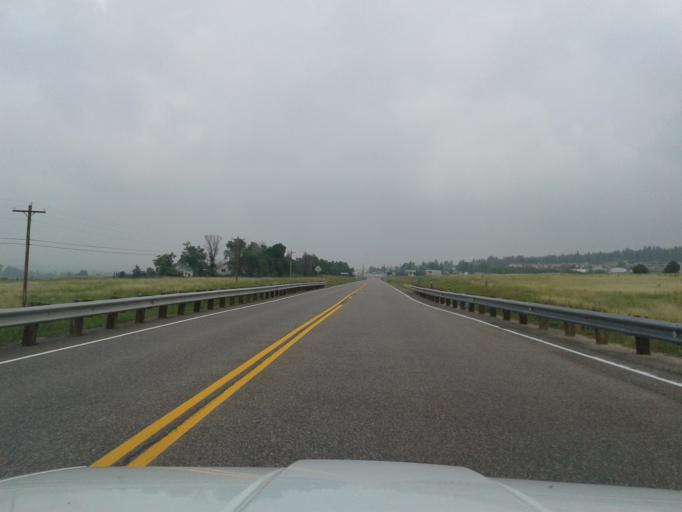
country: US
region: Colorado
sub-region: Douglas County
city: The Pinery
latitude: 39.3842
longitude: -104.7515
